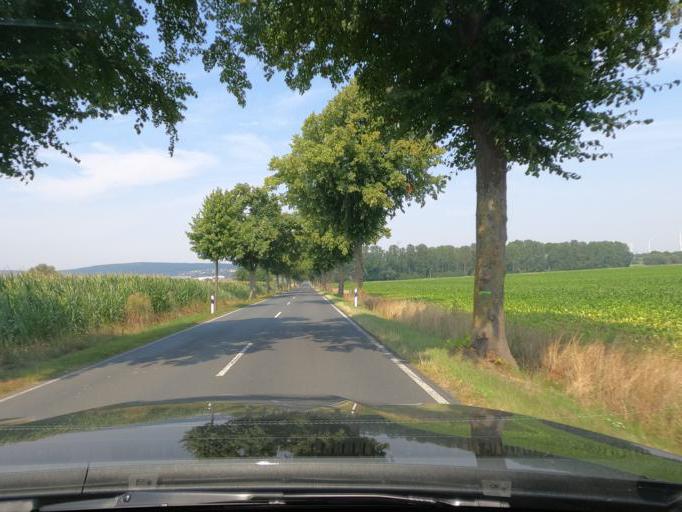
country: DE
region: Lower Saxony
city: Springe
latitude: 52.1906
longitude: 9.6372
